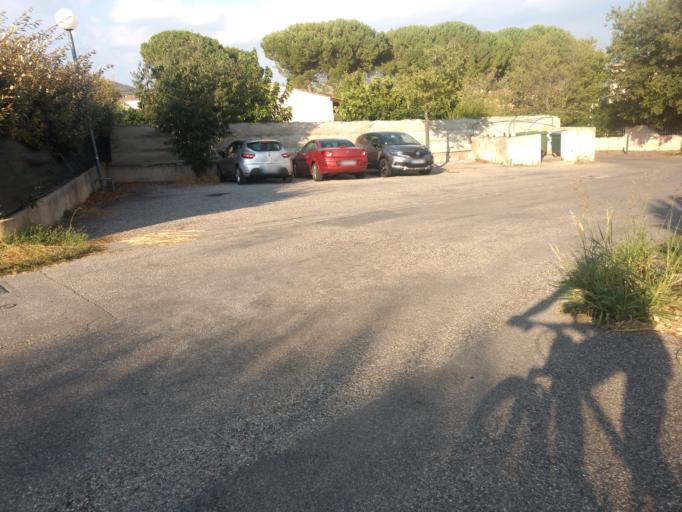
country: FR
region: Provence-Alpes-Cote d'Azur
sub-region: Departement des Alpes-de-Haute-Provence
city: Manosque
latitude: 43.8198
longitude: 5.7749
